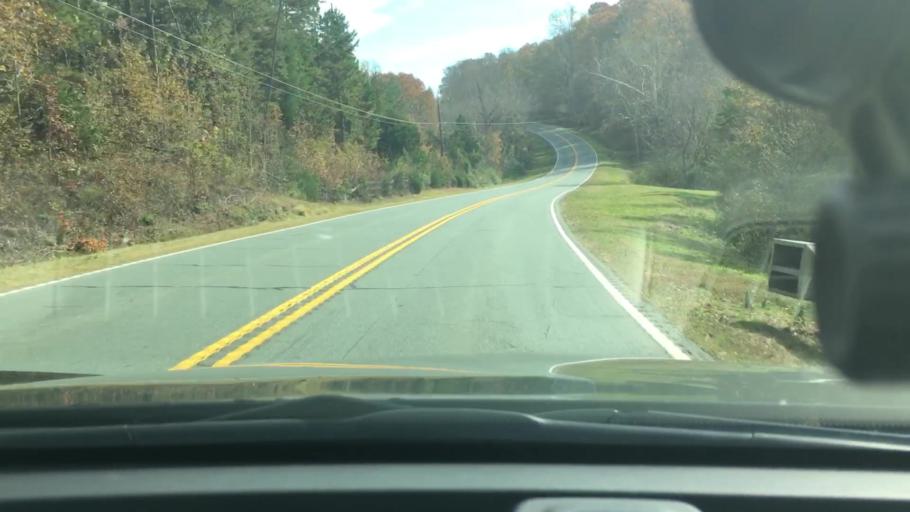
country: US
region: North Carolina
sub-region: Stanly County
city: Badin
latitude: 35.3129
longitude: -80.0918
